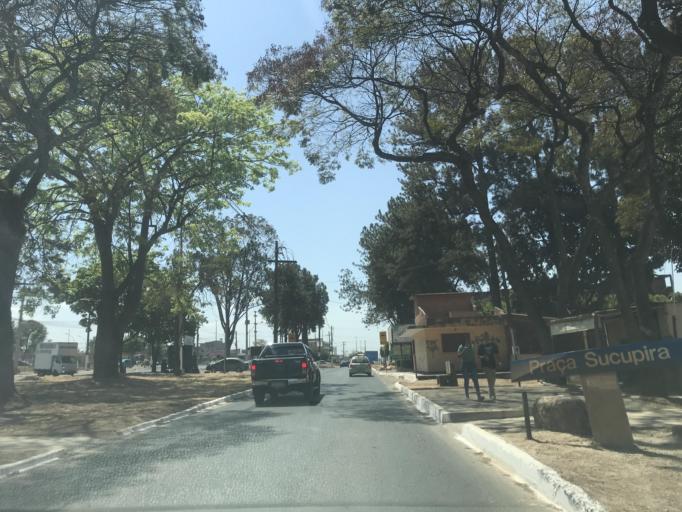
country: BR
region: Federal District
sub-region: Brasilia
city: Brasilia
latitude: -15.8801
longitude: -48.0105
